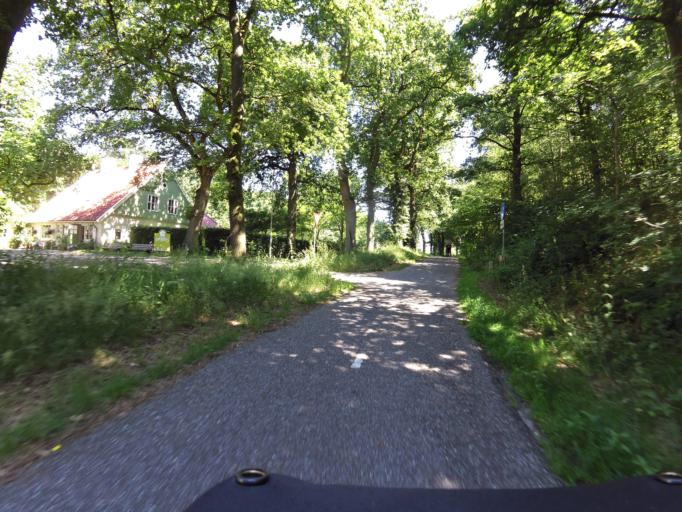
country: NL
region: Overijssel
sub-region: Gemeente Twenterand
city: Magele
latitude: 52.5104
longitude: 6.5156
